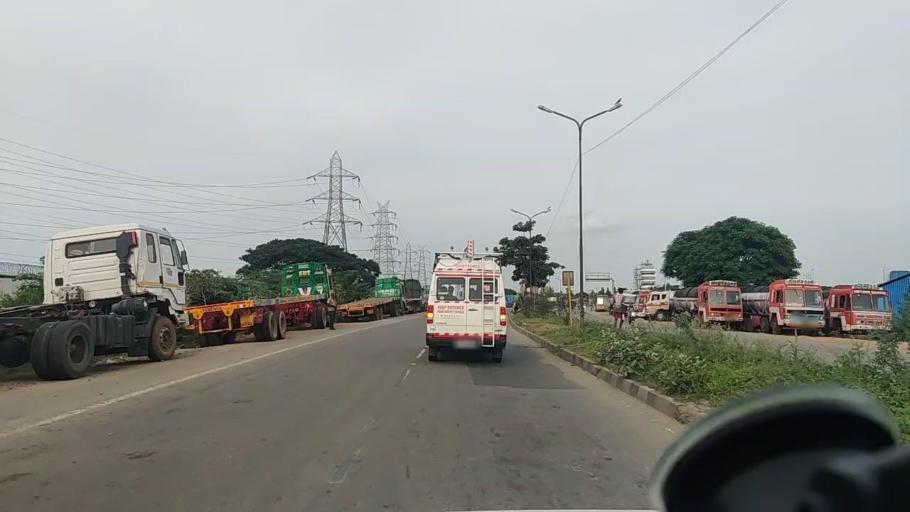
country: IN
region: Tamil Nadu
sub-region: Thiruvallur
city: Chinnasekkadu
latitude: 13.1793
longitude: 80.2523
